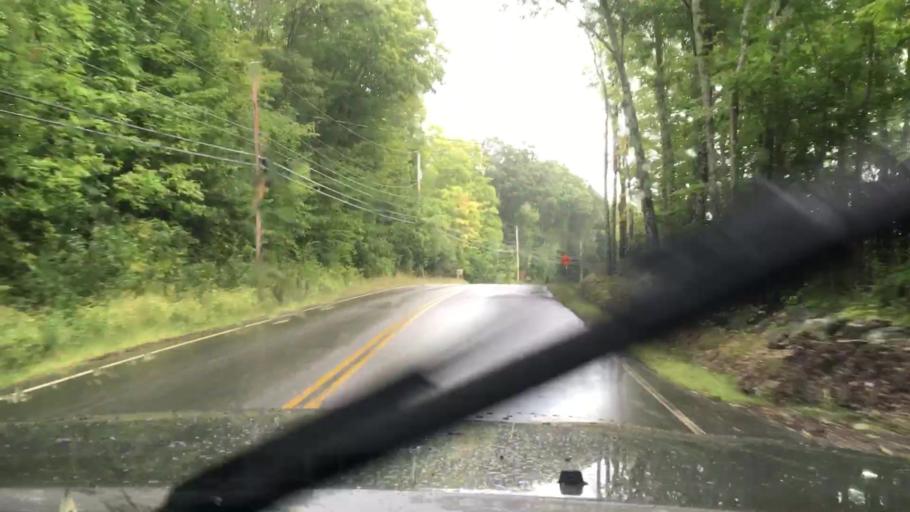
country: US
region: New Hampshire
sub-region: Belknap County
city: Meredith
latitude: 43.6507
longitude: -71.5444
